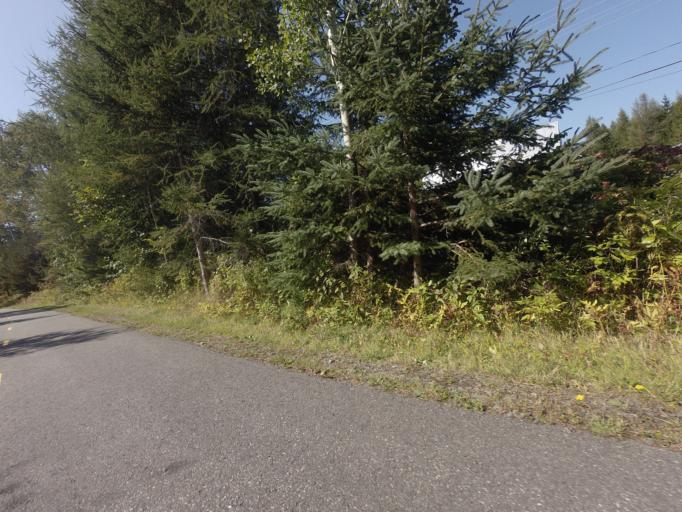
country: CA
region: Quebec
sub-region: Laurentides
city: Mont-Tremblant
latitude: 46.1277
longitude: -74.5653
